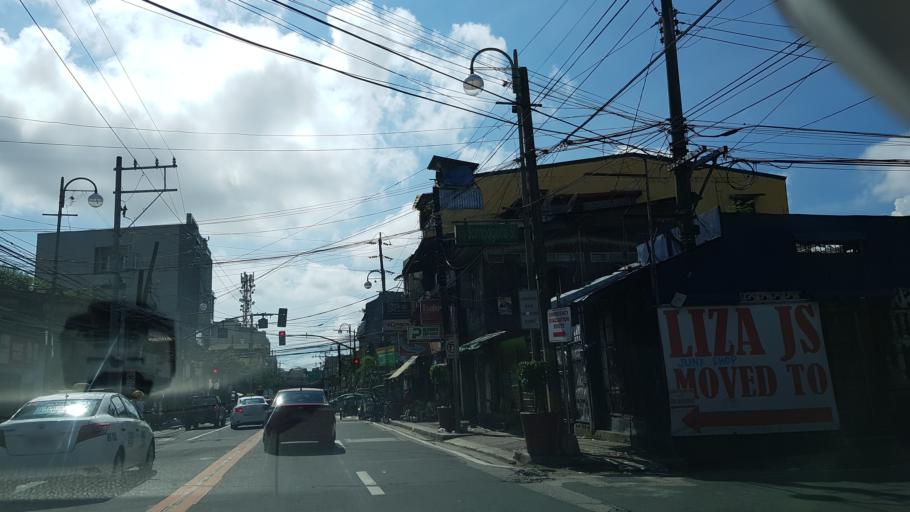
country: PH
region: Metro Manila
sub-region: Makati City
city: Makati City
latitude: 14.5714
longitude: 121.0179
